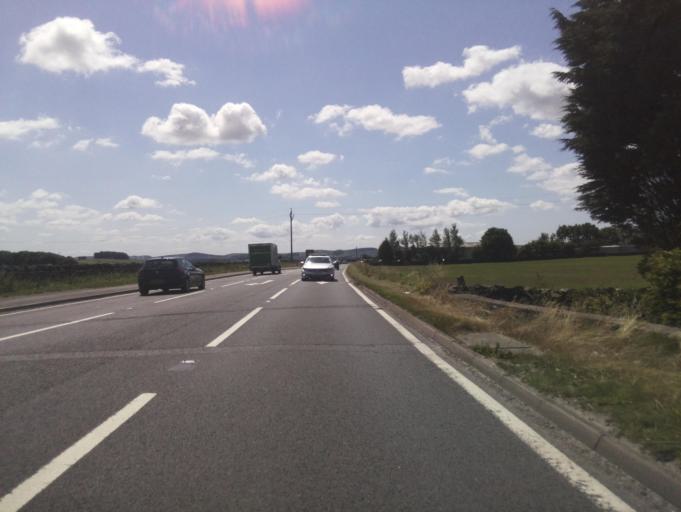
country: GB
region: England
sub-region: Derbyshire
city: Buxton
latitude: 53.2783
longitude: -1.8909
